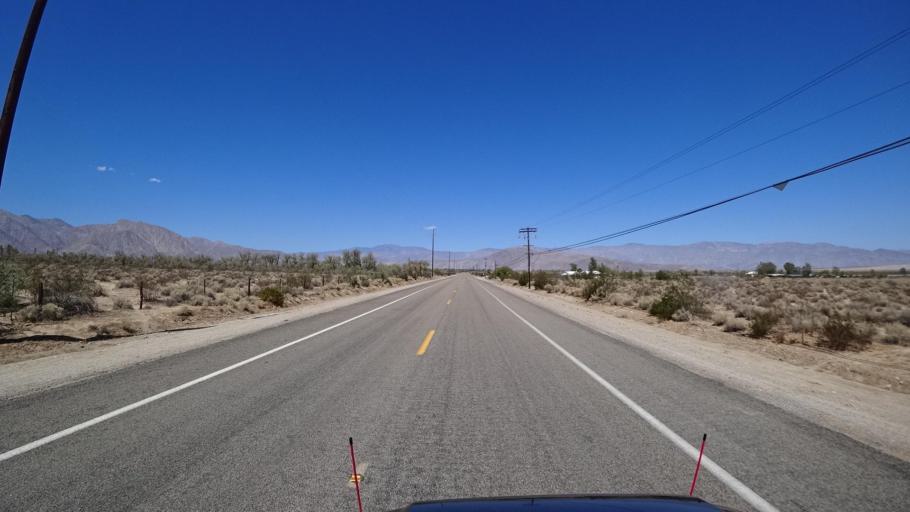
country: US
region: California
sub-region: San Diego County
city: Borrego Springs
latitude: 33.2335
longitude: -116.3479
